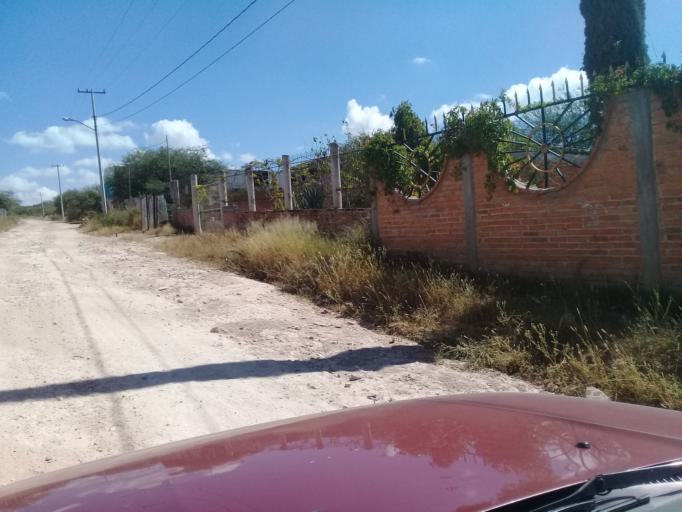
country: MX
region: Aguascalientes
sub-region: Aguascalientes
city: San Sebastian [Fraccionamiento]
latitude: 21.7793
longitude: -102.2569
